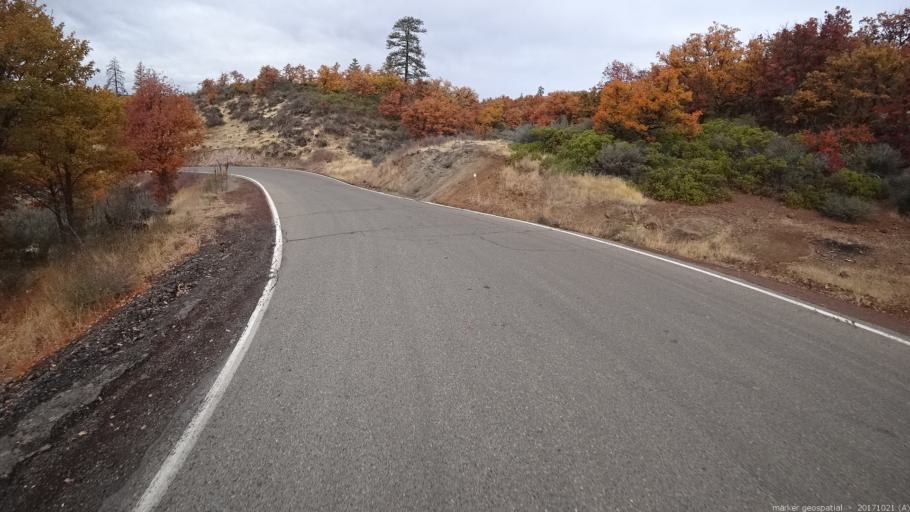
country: US
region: California
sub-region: Shasta County
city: Burney
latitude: 41.0429
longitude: -121.6660
